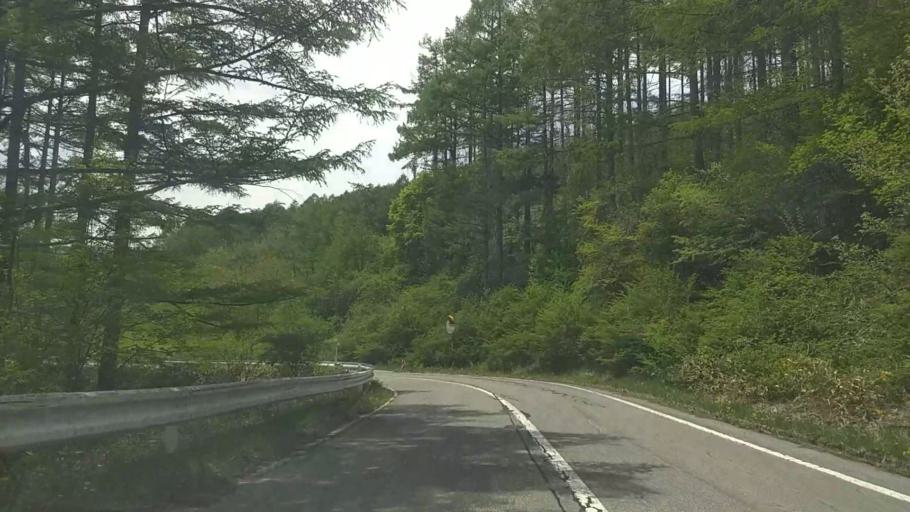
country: JP
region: Nagano
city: Saku
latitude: 36.0895
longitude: 138.3892
